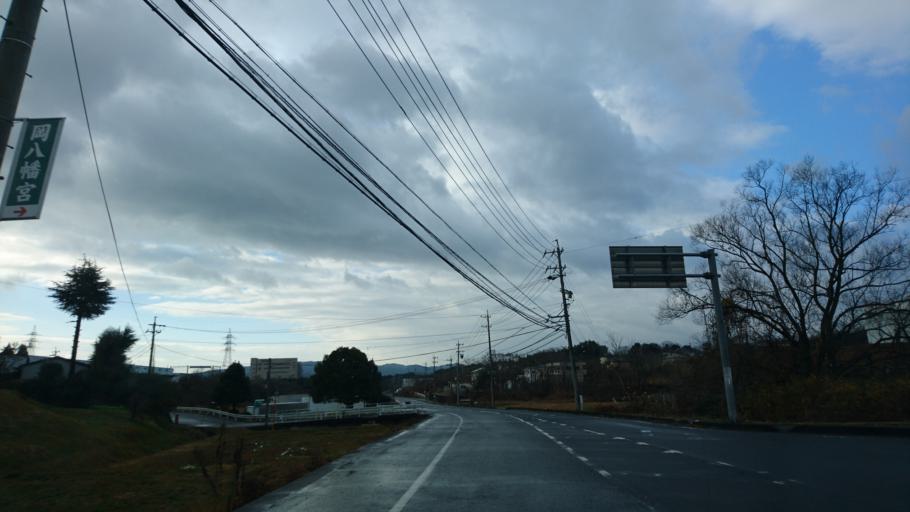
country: JP
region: Mie
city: Ueno-ebisumachi
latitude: 34.7251
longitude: 136.0819
